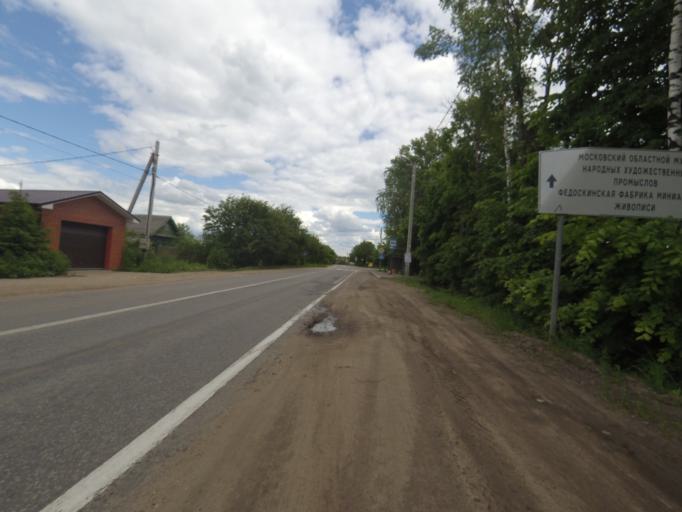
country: RU
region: Moskovskaya
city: Marfino
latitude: 56.0494
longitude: 37.5729
